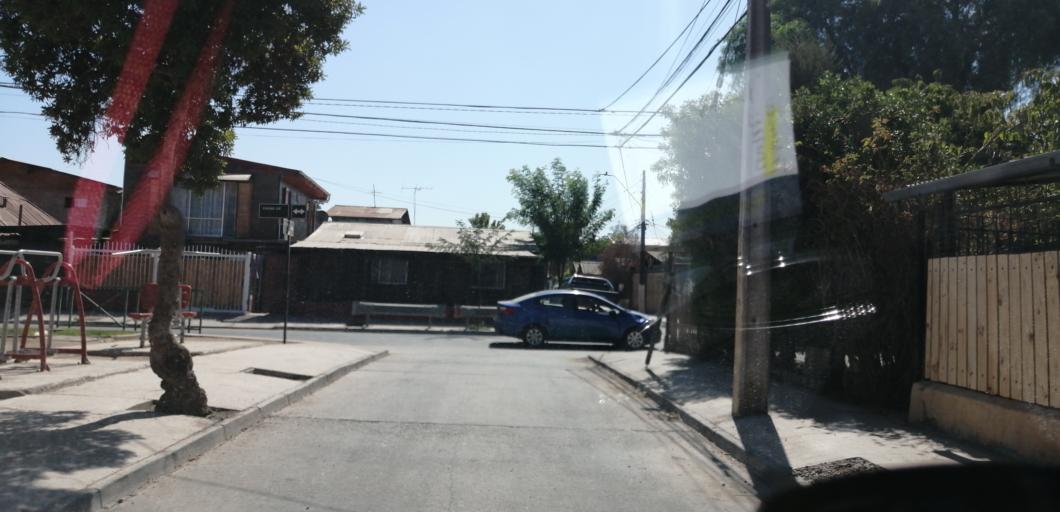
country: CL
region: Santiago Metropolitan
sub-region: Provincia de Santiago
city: Lo Prado
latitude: -33.4350
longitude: -70.7537
